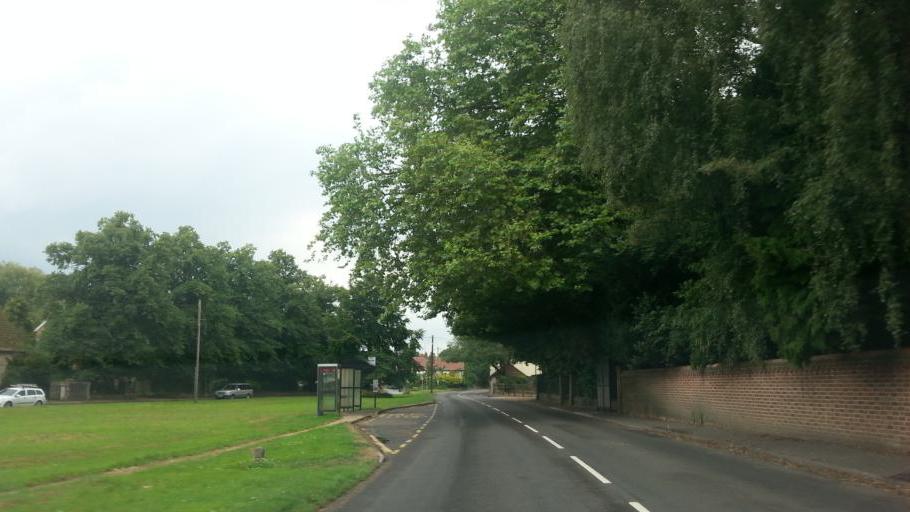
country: GB
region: England
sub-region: Norfolk
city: Fakenham
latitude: 52.8203
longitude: 0.7100
